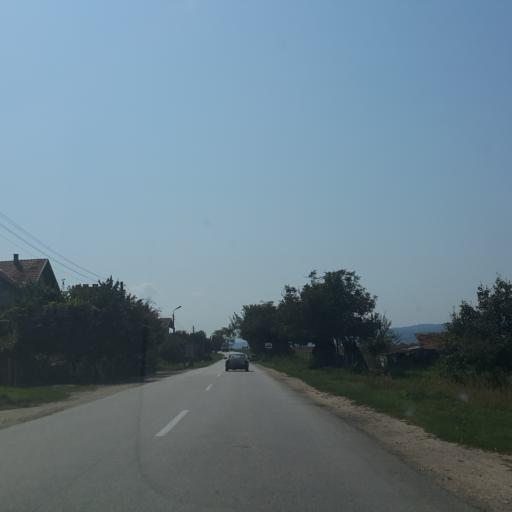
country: RS
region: Central Serbia
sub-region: Zajecarski Okrug
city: Knjazevac
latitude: 43.6801
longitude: 22.2907
